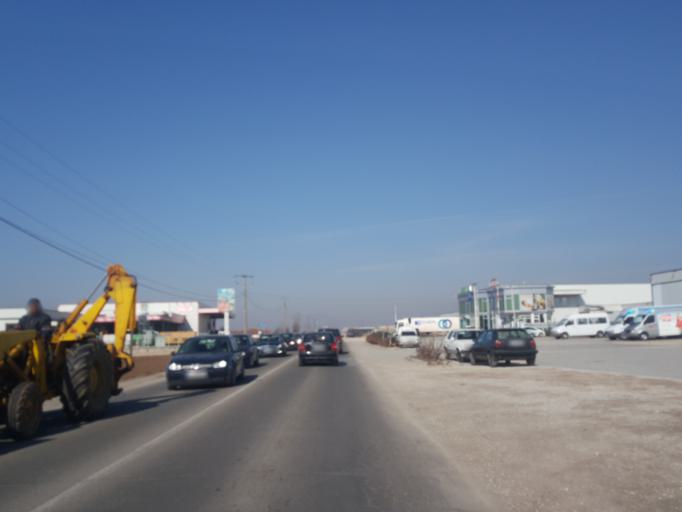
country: XK
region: Mitrovica
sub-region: Vushtrri
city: Vushtrri
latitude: 42.7835
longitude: 21.0109
